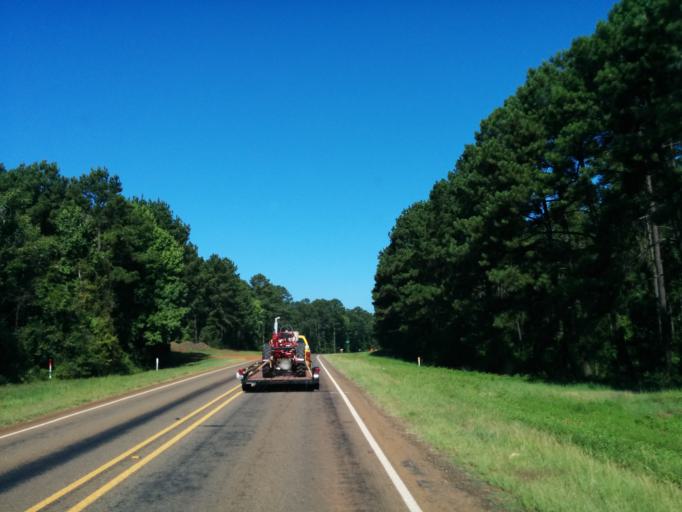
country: US
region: Texas
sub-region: Sabine County
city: Milam
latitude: 31.4291
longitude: -93.8080
